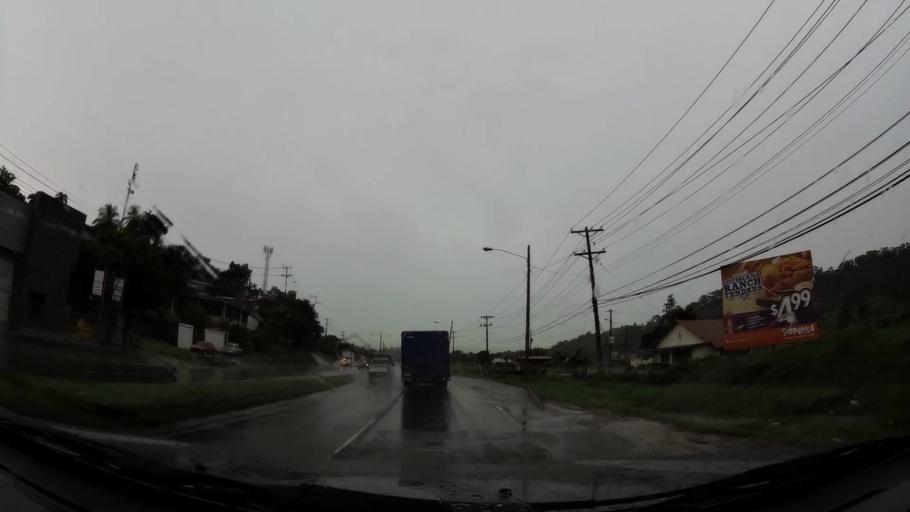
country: PA
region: Colon
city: Cativa
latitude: 9.3589
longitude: -79.8194
